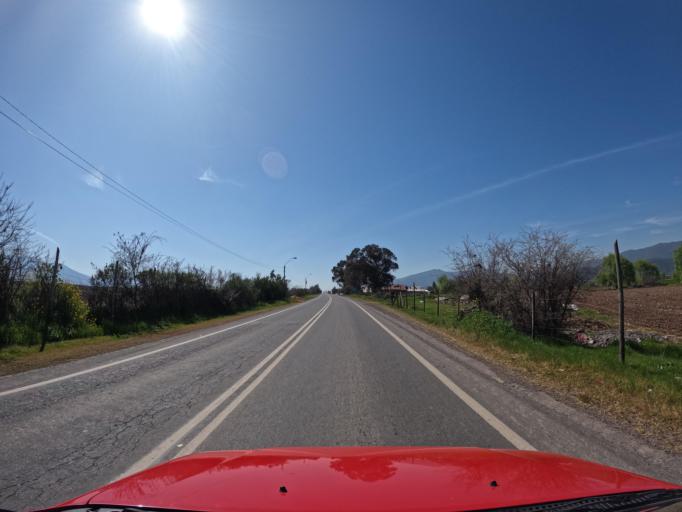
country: CL
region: Maule
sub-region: Provincia de Curico
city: Rauco
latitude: -35.0457
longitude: -71.4636
